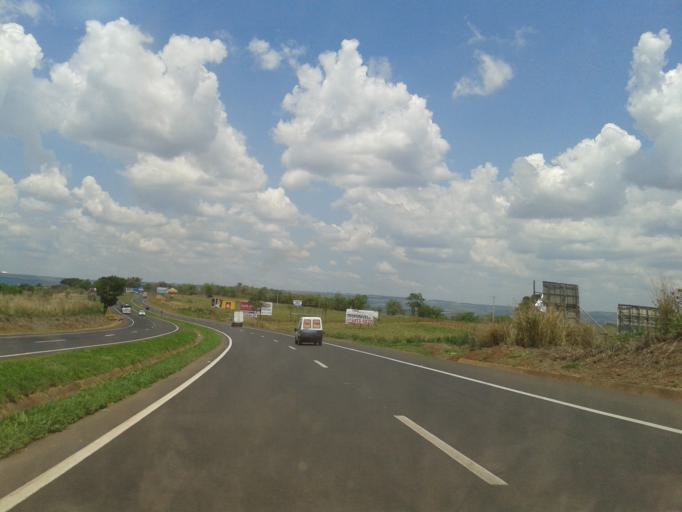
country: BR
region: Minas Gerais
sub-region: Araguari
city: Araguari
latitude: -18.7310
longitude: -48.2228
